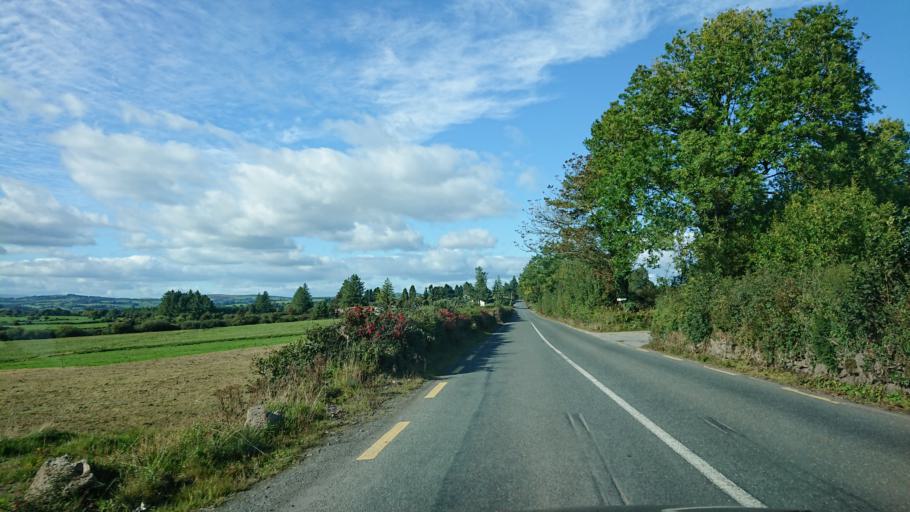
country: IE
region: Munster
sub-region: Waterford
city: Dungarvan
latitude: 52.1899
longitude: -7.6972
